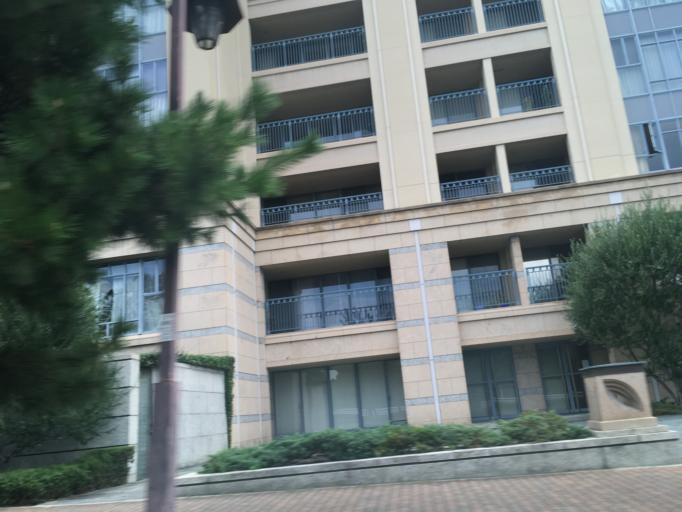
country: JP
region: Hyogo
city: Ashiya
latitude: 34.7228
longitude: 135.2647
